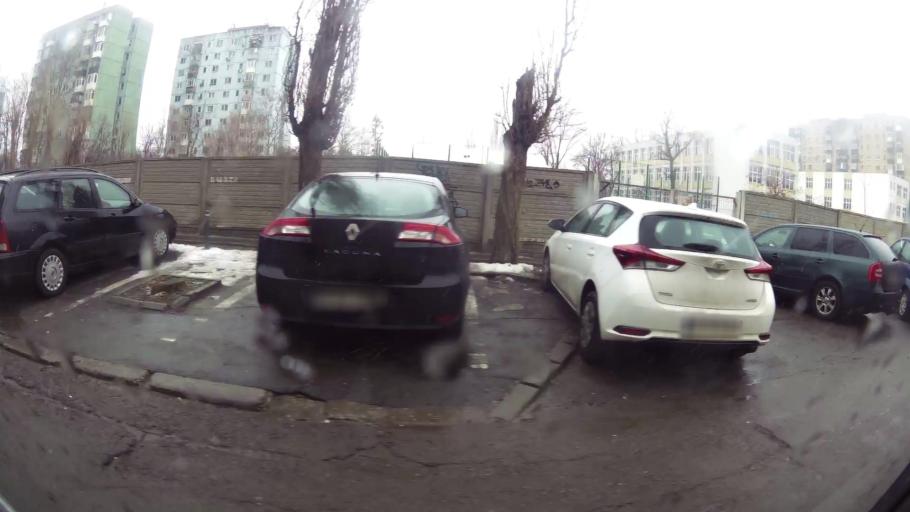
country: RO
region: Ilfov
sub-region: Comuna Chiajna
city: Rosu
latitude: 44.4139
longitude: 26.0242
